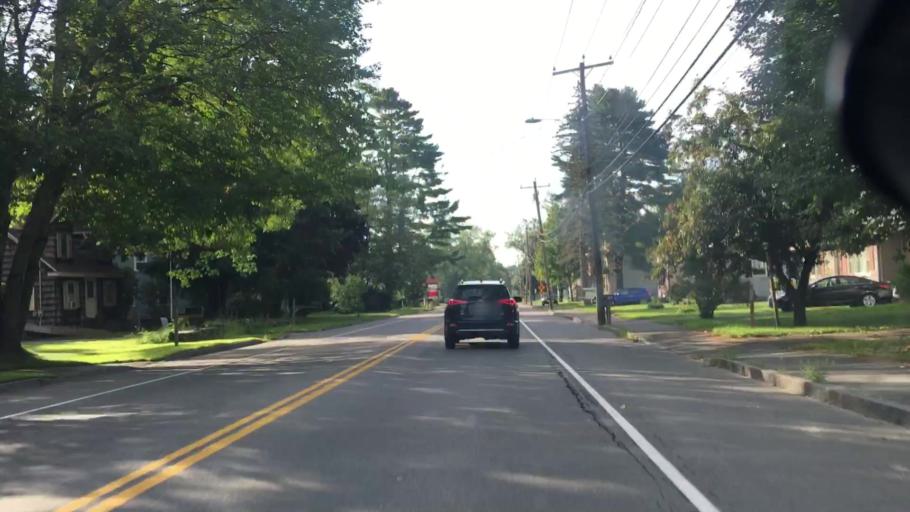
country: US
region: Maine
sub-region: Cumberland County
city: Westbrook
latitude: 43.7081
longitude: -70.3286
